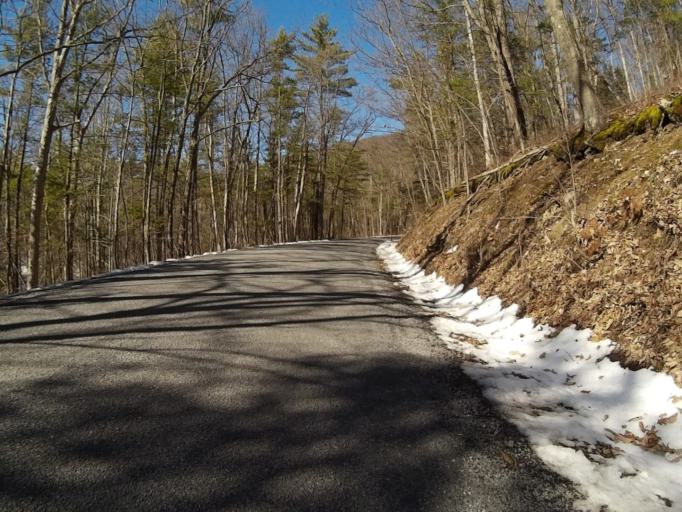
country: US
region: Pennsylvania
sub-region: Centre County
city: Stormstown
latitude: 40.8417
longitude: -78.0252
